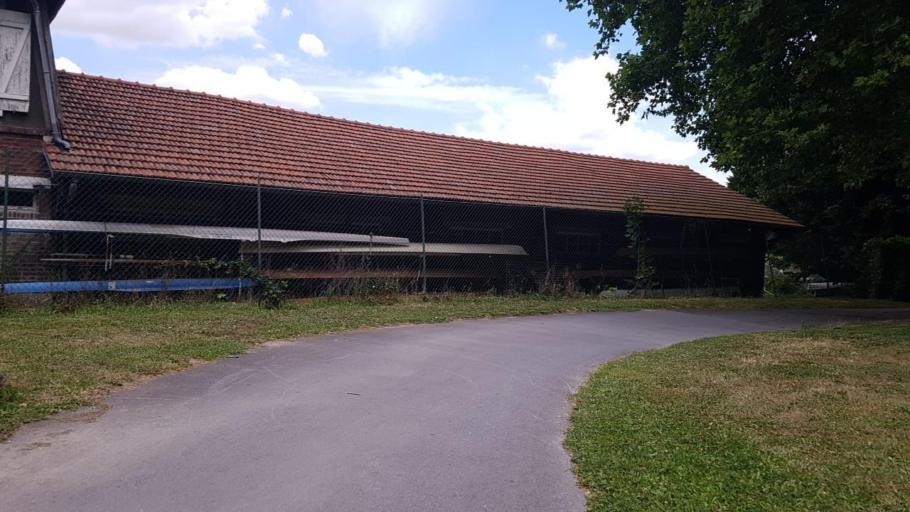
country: FR
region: Picardie
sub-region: Departement de l'Oise
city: Compiegne
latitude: 49.4233
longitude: 2.8306
